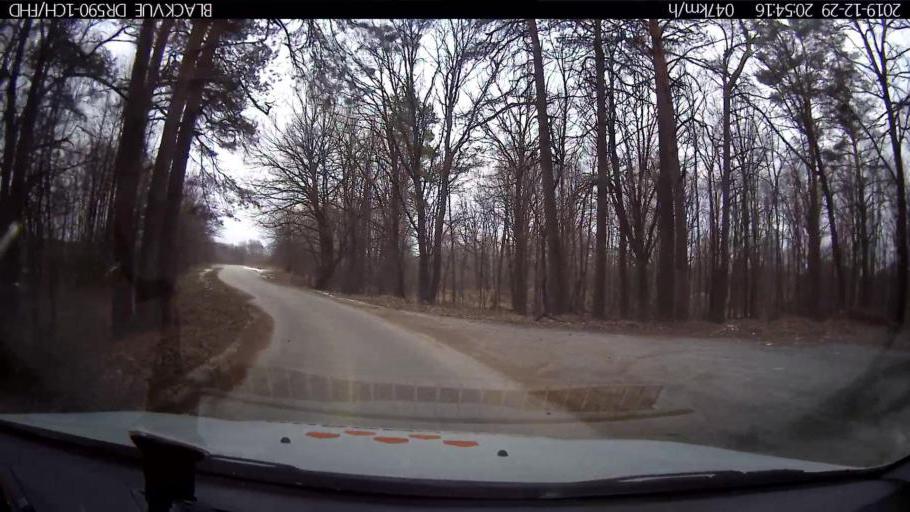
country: RU
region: Nizjnij Novgorod
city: Afonino
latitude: 56.1653
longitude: 43.9881
